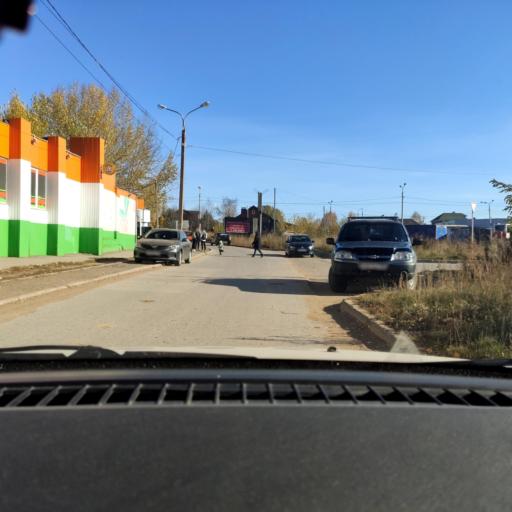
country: RU
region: Perm
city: Perm
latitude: 58.0544
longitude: 56.3532
